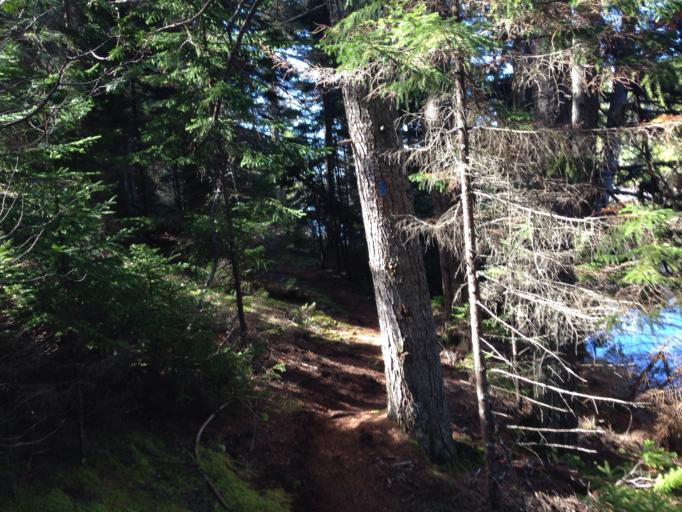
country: US
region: Maine
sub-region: Hancock County
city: Gouldsboro
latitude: 44.3888
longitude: -68.0744
